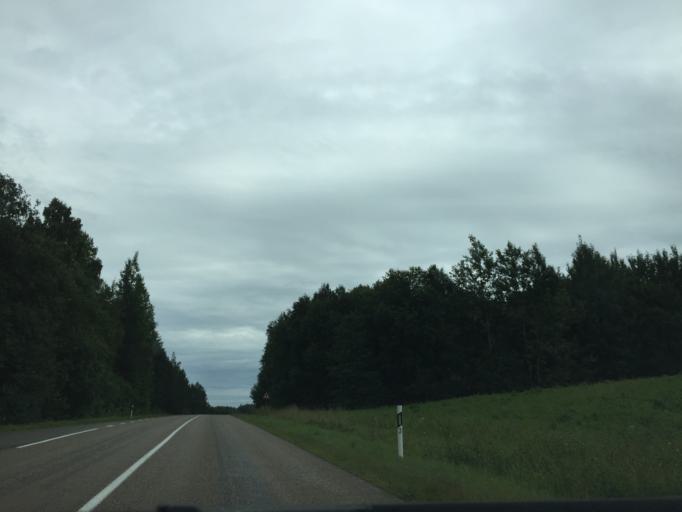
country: LV
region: Dagda
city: Dagda
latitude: 56.1883
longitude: 27.3523
